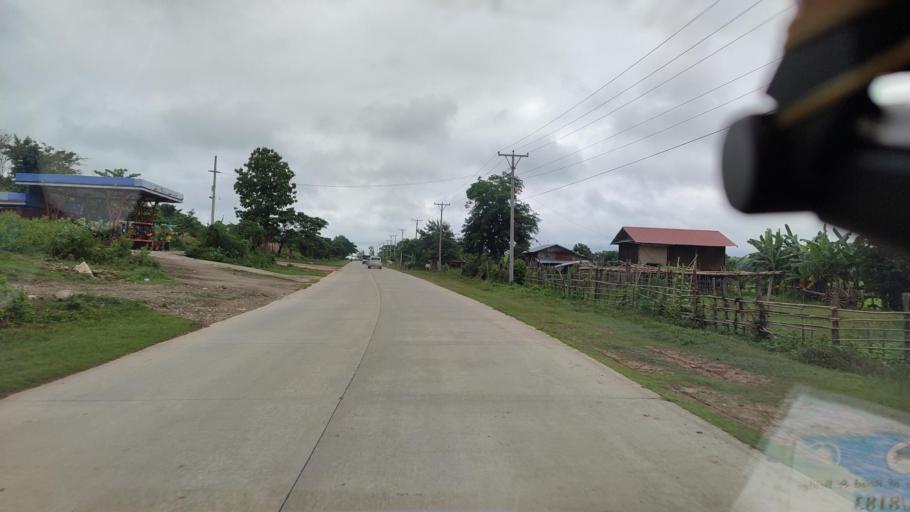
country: MM
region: Mandalay
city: Nay Pyi Taw
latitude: 19.8799
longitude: 96.0252
